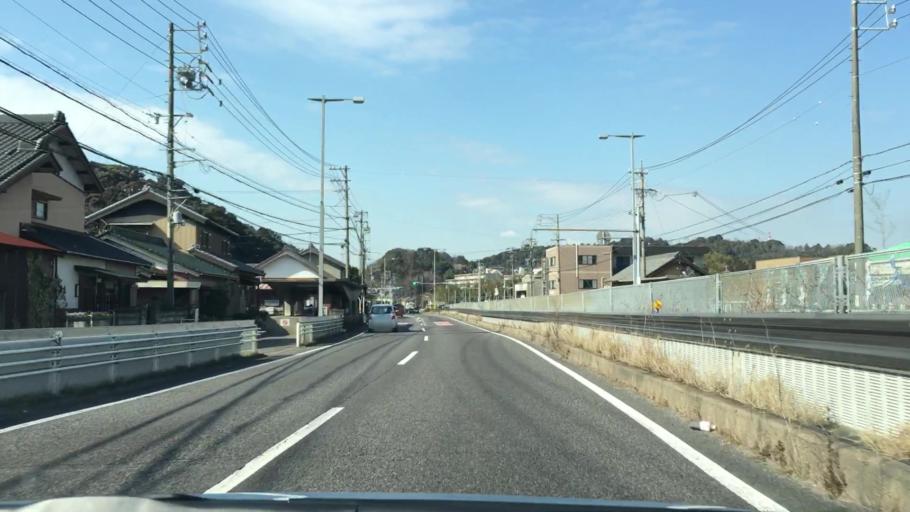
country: JP
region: Aichi
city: Gamagori
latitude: 34.8961
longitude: 137.2514
